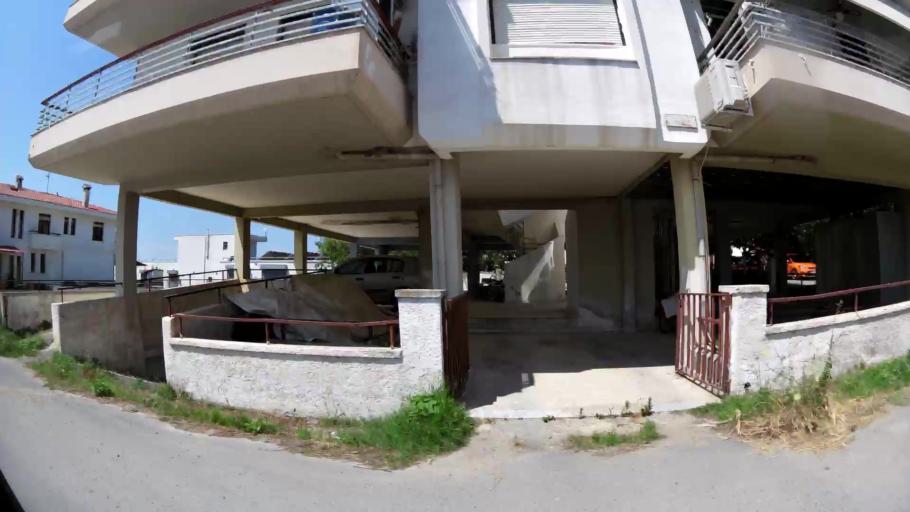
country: GR
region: Central Macedonia
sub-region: Nomos Thessalonikis
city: Nea Michaniona
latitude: 40.4964
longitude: 22.8191
